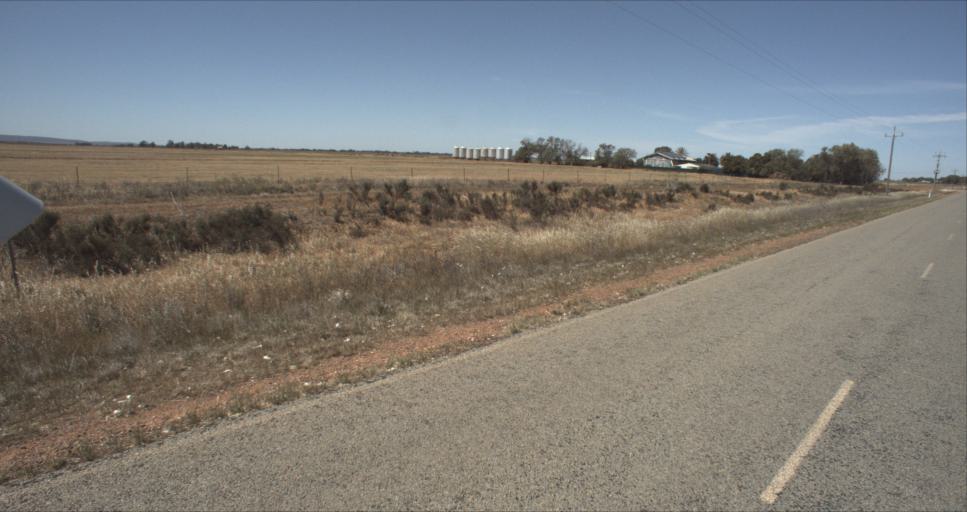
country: AU
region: New South Wales
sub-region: Leeton
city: Leeton
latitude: -34.4498
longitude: 146.2962
